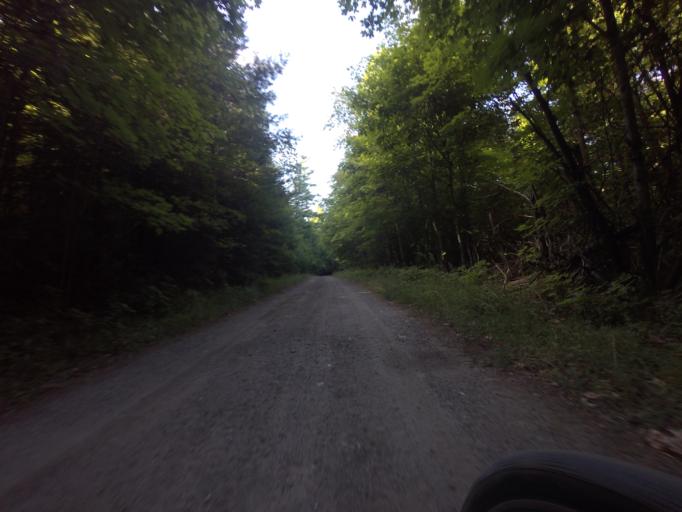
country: CA
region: Ontario
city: Arnprior
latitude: 45.1879
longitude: -76.5141
